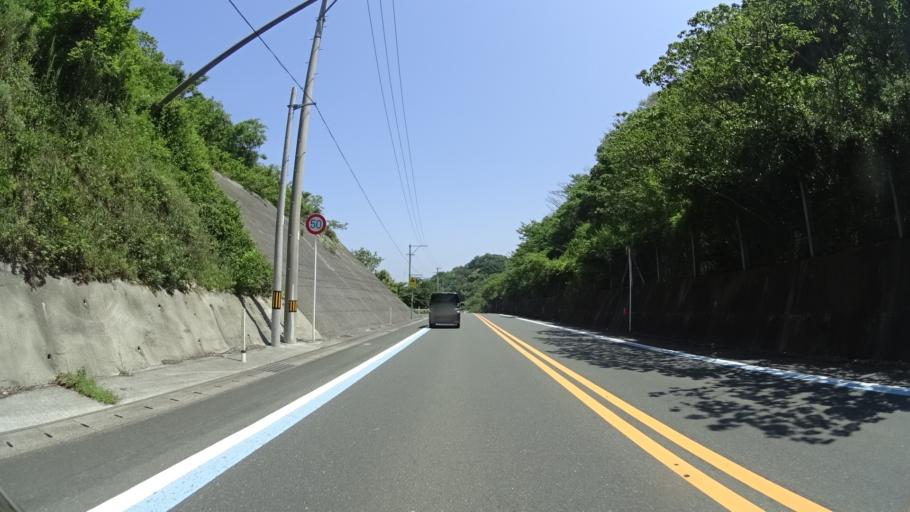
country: JP
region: Ehime
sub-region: Nishiuwa-gun
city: Ikata-cho
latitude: 33.5371
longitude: 132.4016
